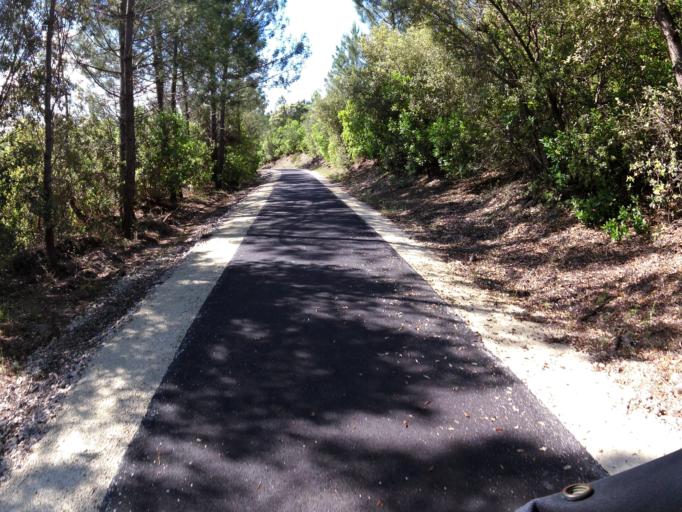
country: FR
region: Aquitaine
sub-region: Departement de la Gironde
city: Lacanau
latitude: 45.0308
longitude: -1.1760
